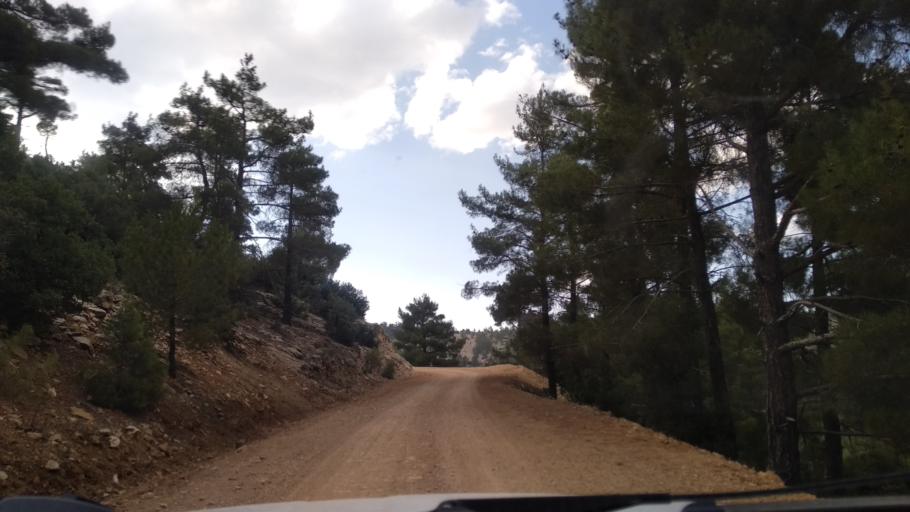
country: TR
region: Mersin
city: Sarikavak
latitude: 36.5979
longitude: 33.7046
